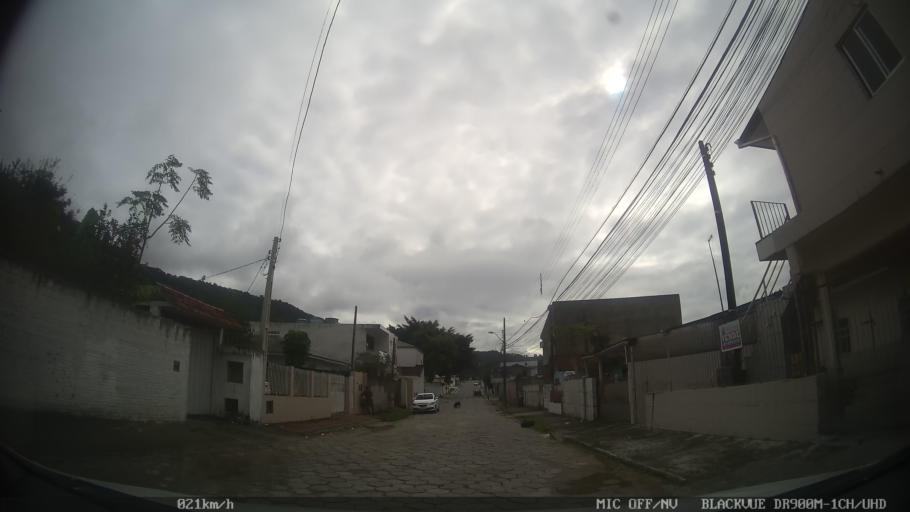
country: BR
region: Santa Catarina
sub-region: Biguacu
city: Biguacu
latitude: -27.5481
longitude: -48.6452
